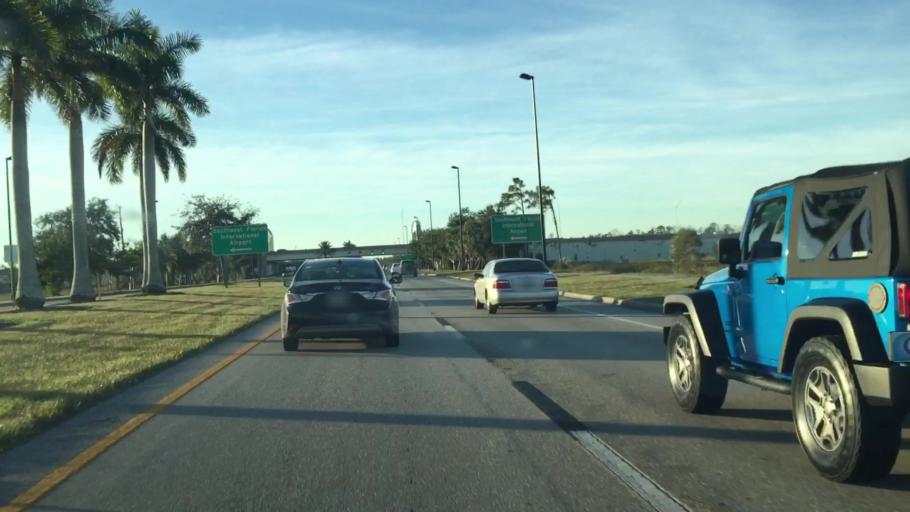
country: US
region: Florida
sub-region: Lee County
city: Three Oaks
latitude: 26.5146
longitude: -81.7856
